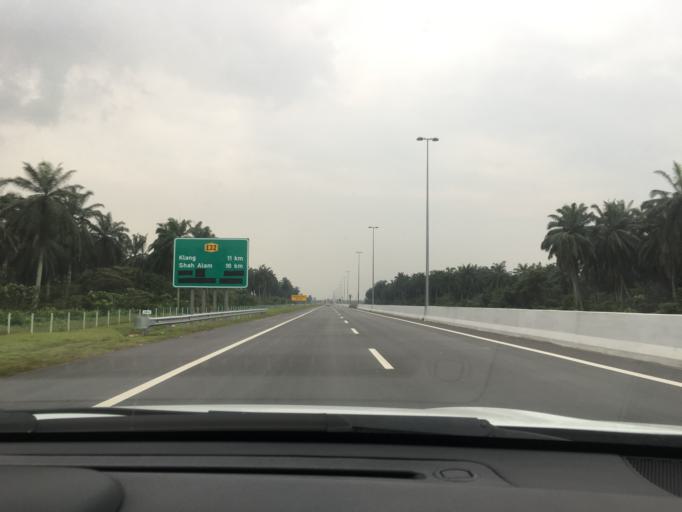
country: MY
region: Selangor
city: Klang
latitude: 3.1194
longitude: 101.4092
